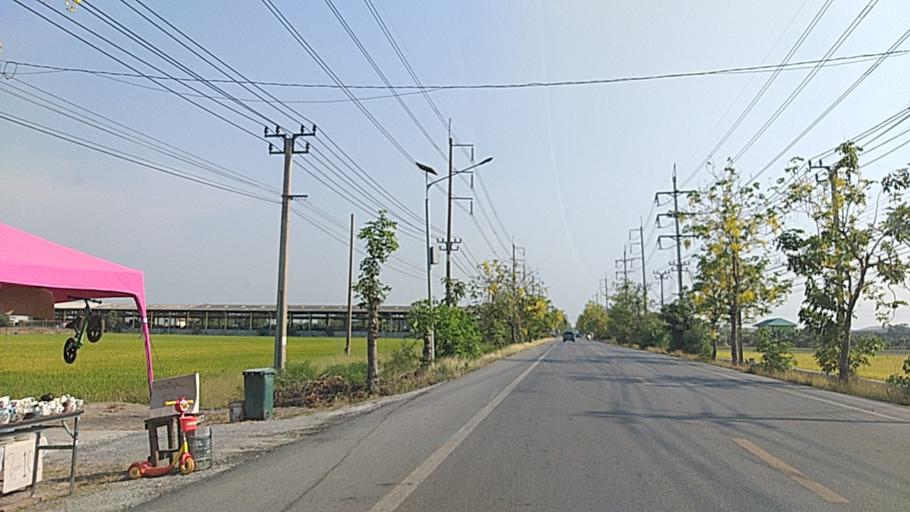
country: TH
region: Nonthaburi
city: Sai Noi
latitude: 14.0361
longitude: 100.3123
